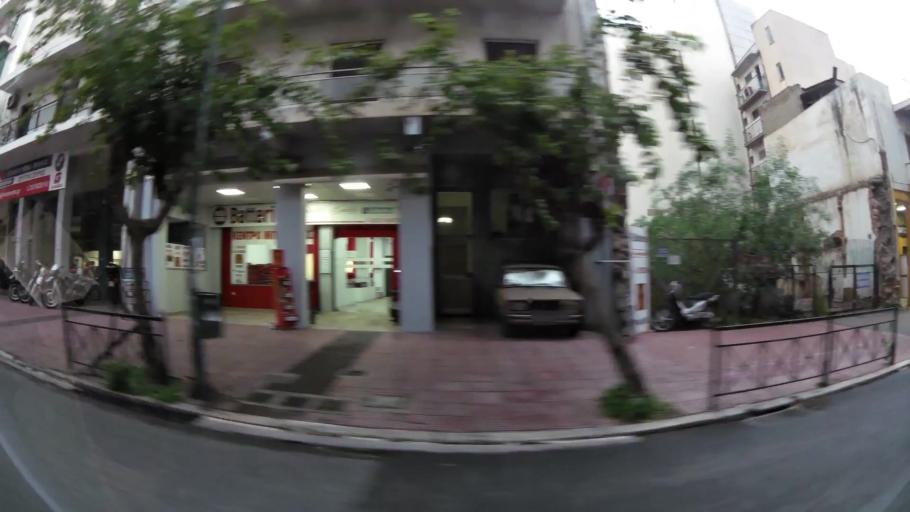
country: GR
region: Attica
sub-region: Nomarchia Athinas
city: Dhafni
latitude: 37.9587
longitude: 23.7343
